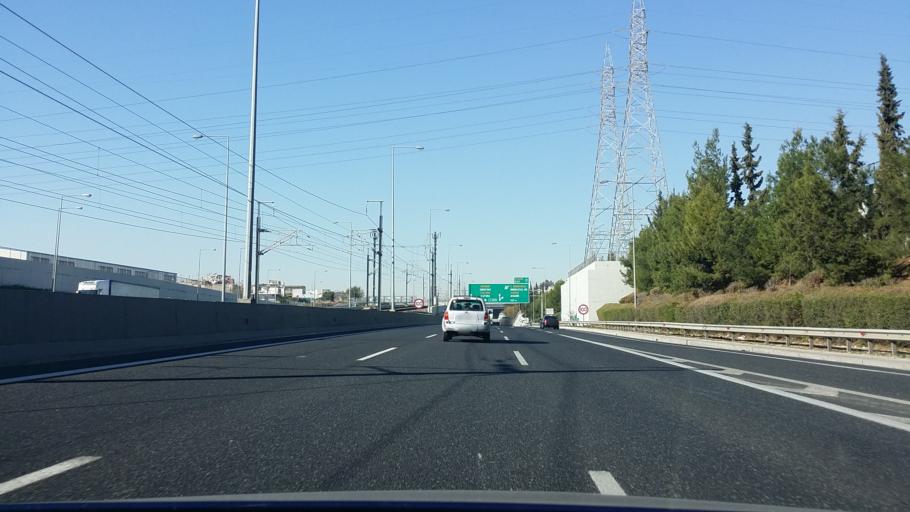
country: GR
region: Attica
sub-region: Nomarchia Athinas
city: Metamorfosi
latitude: 38.0637
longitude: 23.7447
